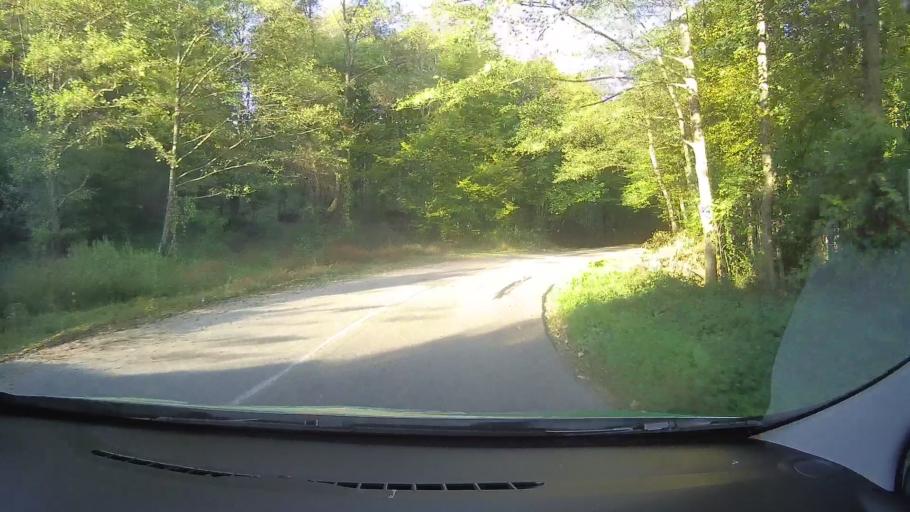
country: RO
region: Timis
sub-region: Comuna Nadrag
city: Nadrag
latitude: 45.6696
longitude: 22.1655
